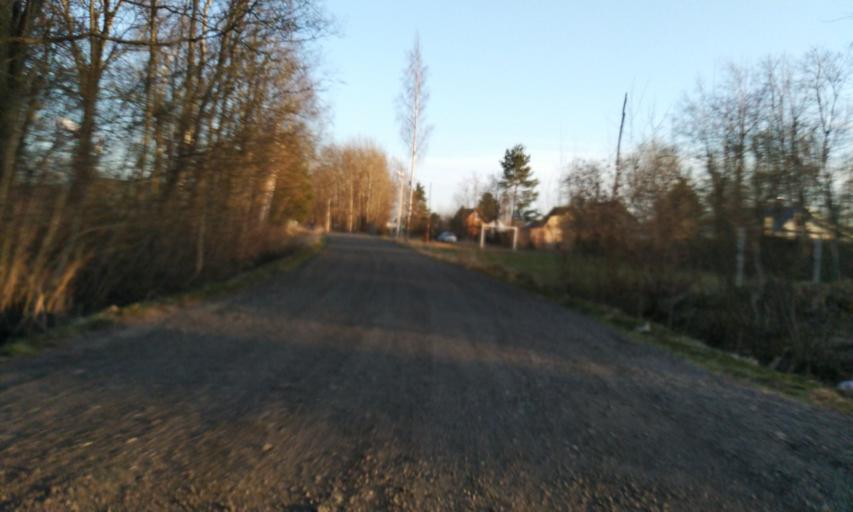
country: RU
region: Leningrad
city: Novoye Devyatkino
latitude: 60.0883
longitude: 30.4569
